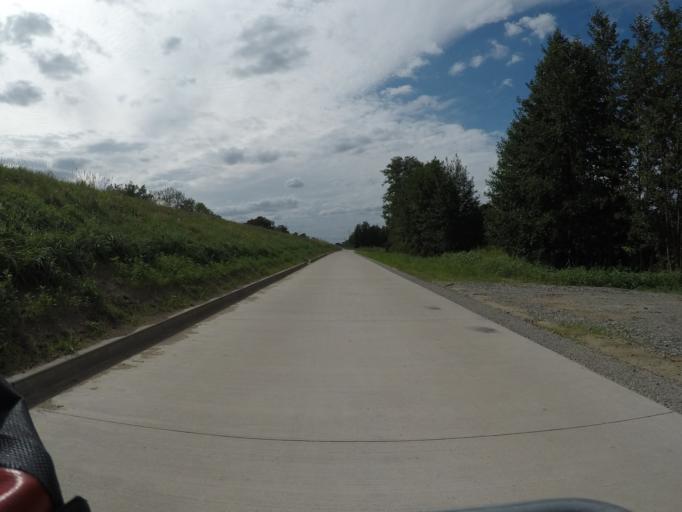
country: DE
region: Lower Saxony
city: Handorf
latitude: 53.3556
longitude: 10.3572
